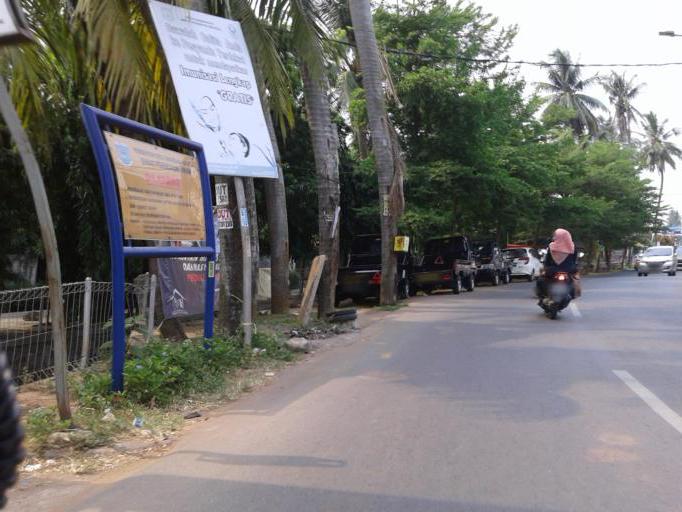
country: ID
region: West Java
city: Pamulang
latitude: -6.3161
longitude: 106.7588
